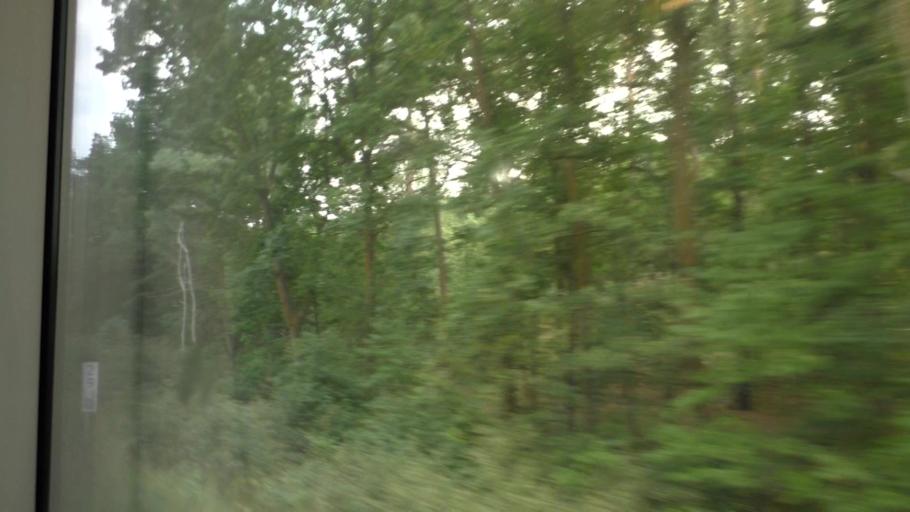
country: DE
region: Brandenburg
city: Wendisch Rietz
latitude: 52.2122
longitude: 14.0021
